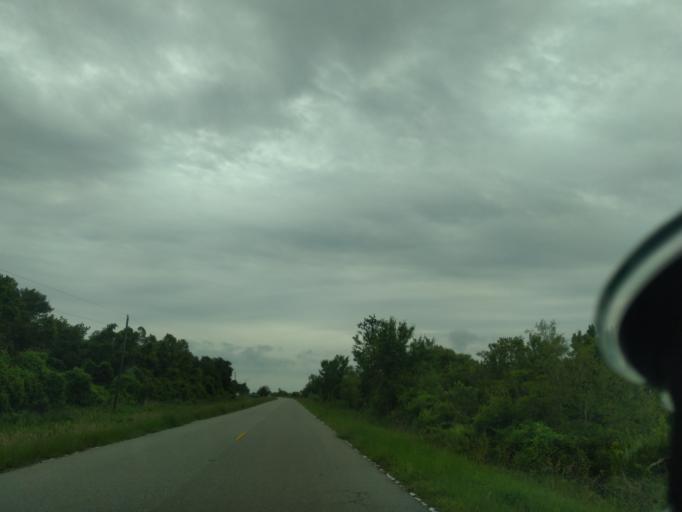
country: US
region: North Carolina
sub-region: Beaufort County
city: Belhaven
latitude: 35.7469
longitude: -76.4978
